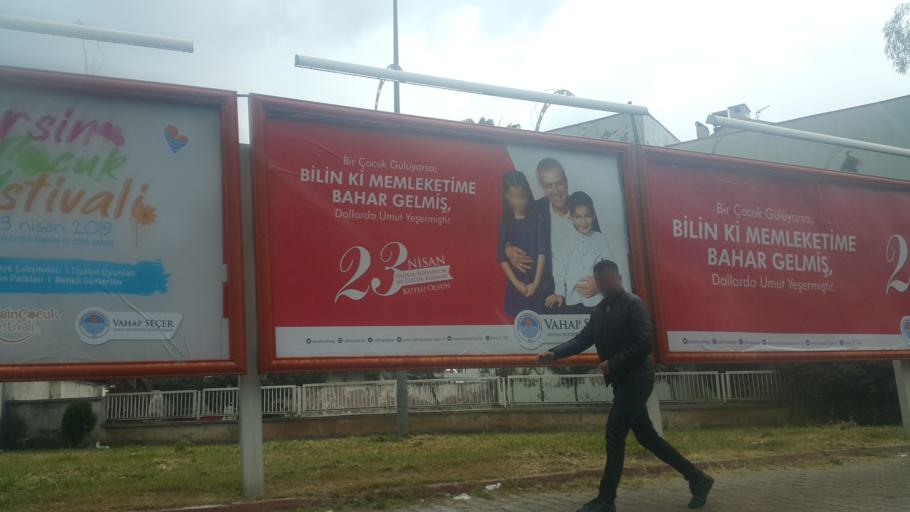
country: TR
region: Mersin
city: Mercin
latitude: 36.8009
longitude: 34.6359
